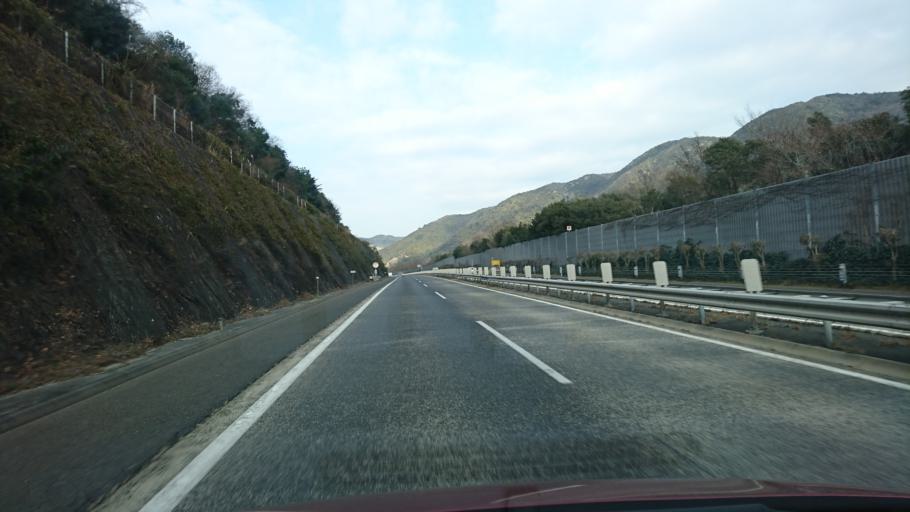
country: JP
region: Hyogo
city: Kariya
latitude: 34.7748
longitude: 134.3596
